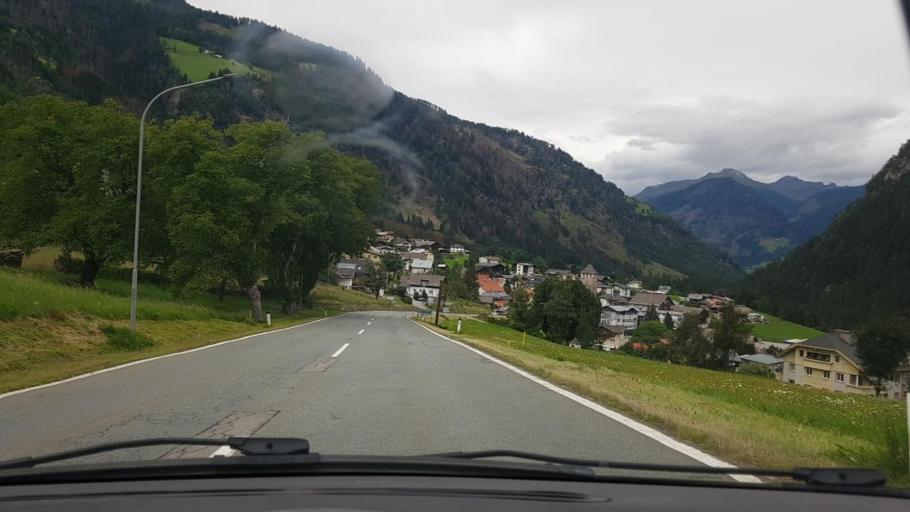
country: AT
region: Carinthia
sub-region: Politischer Bezirk Spittal an der Drau
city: Winklern
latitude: 46.8669
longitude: 12.8756
